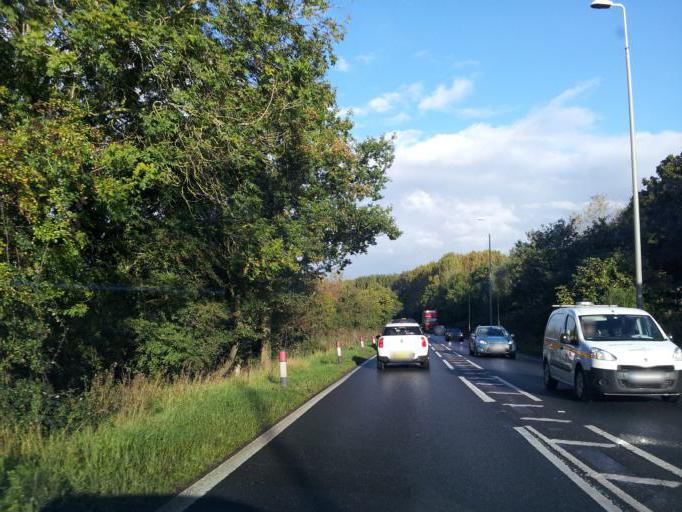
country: GB
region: England
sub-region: Norfolk
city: Hethersett
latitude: 52.6603
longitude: 1.1171
